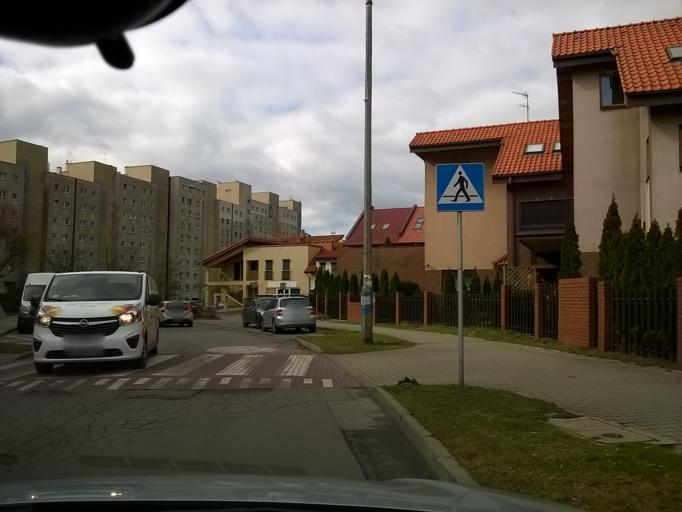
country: PL
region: Silesian Voivodeship
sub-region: Chorzow
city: Chorzow
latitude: 50.2865
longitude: 18.9564
